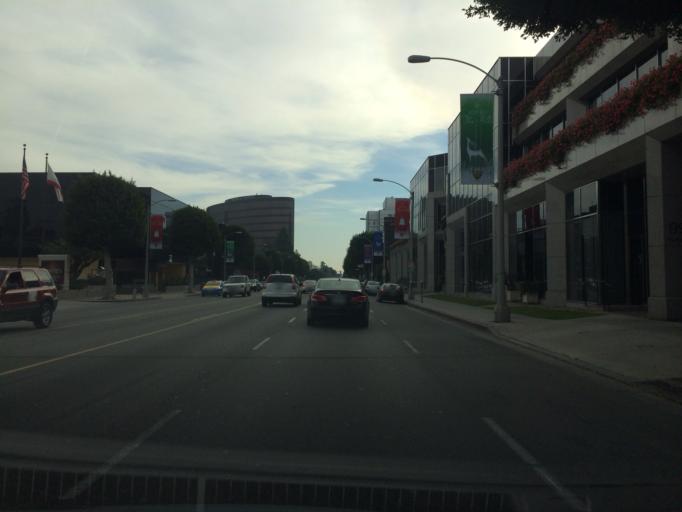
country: US
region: California
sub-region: Los Angeles County
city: Beverly Hills
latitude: 34.0680
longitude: -118.3764
